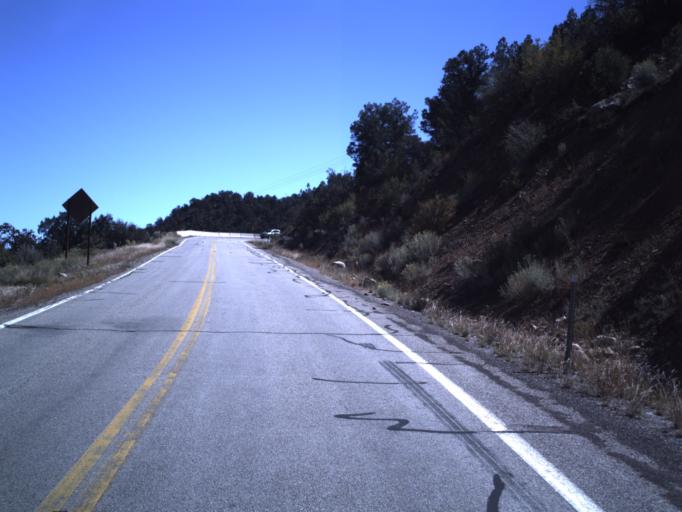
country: US
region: Utah
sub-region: Grand County
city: Moab
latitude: 38.3292
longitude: -109.0949
